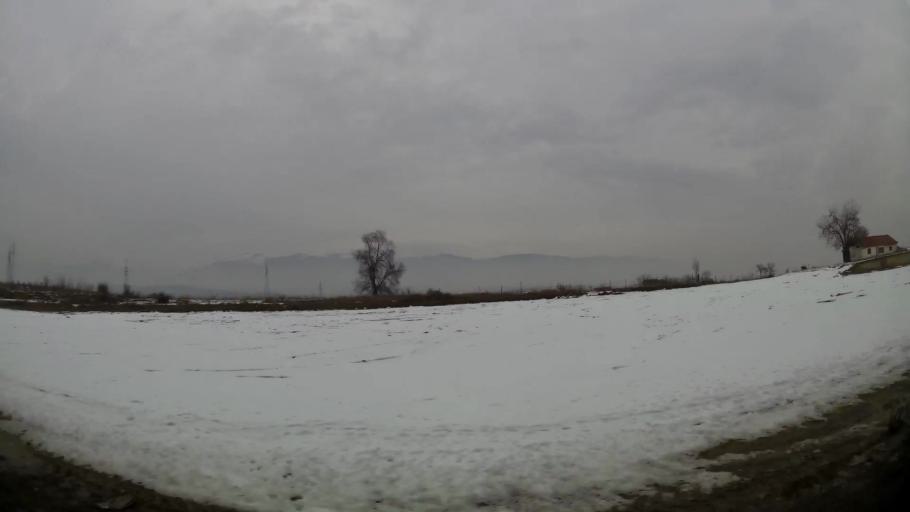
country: MK
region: Suto Orizari
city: Suto Orizare
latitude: 42.0421
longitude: 21.4378
